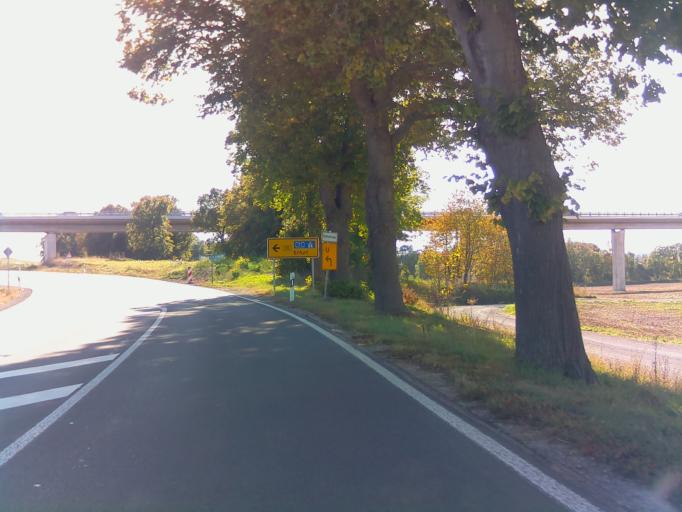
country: DE
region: Thuringia
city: Stadtilm
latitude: 50.7619
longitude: 11.0575
